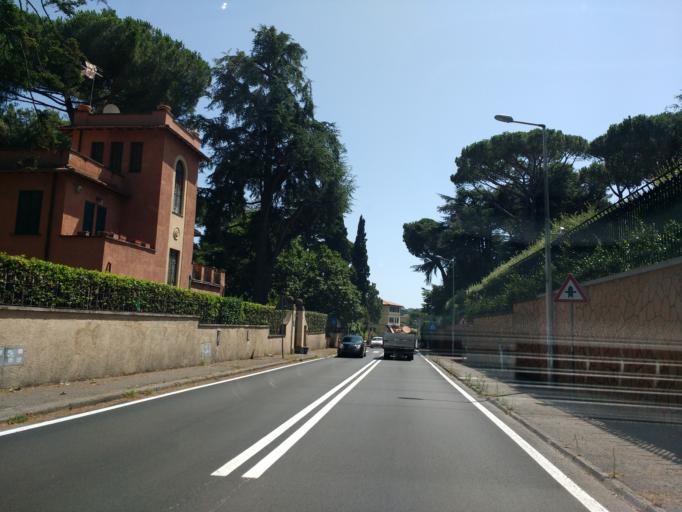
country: IT
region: Latium
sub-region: Citta metropolitana di Roma Capitale
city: Grottaferrata
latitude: 41.7862
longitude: 12.6815
